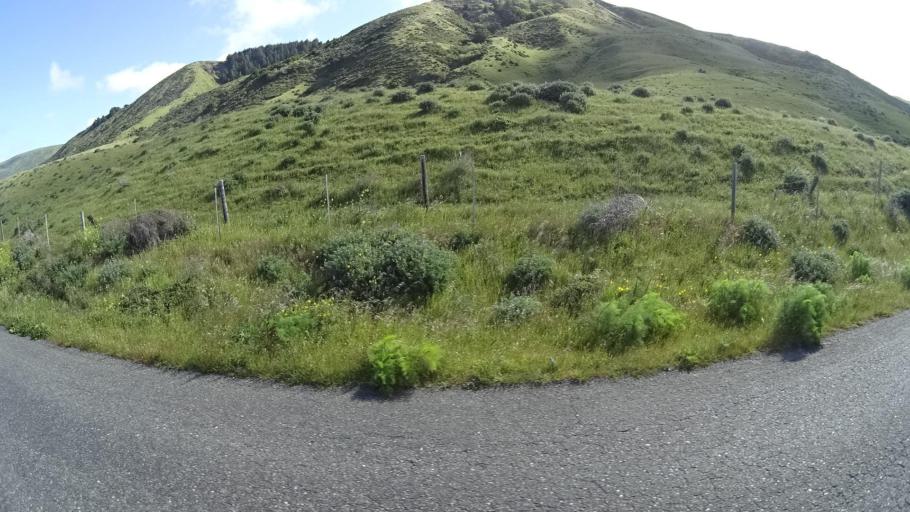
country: US
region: California
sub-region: Humboldt County
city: Ferndale
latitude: 40.4154
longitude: -124.3969
